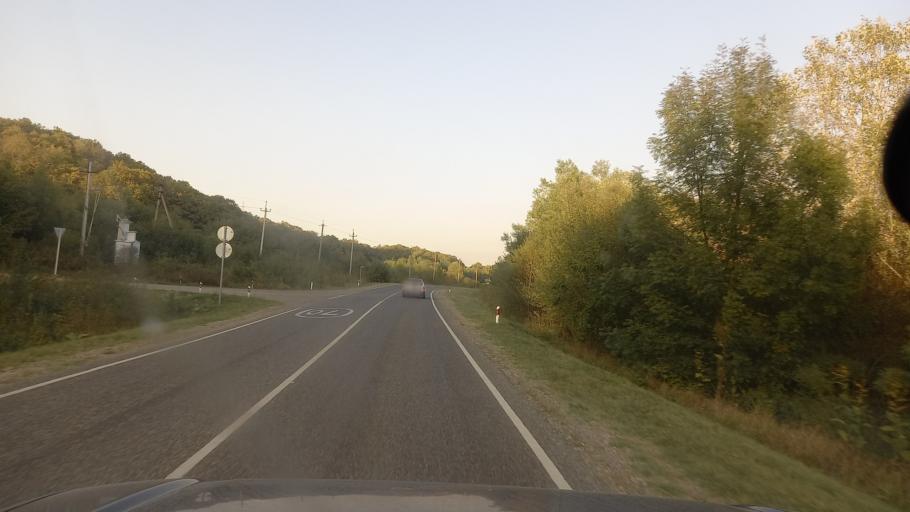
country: RU
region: Krasnodarskiy
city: Smolenskaya
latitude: 44.7460
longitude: 38.7527
